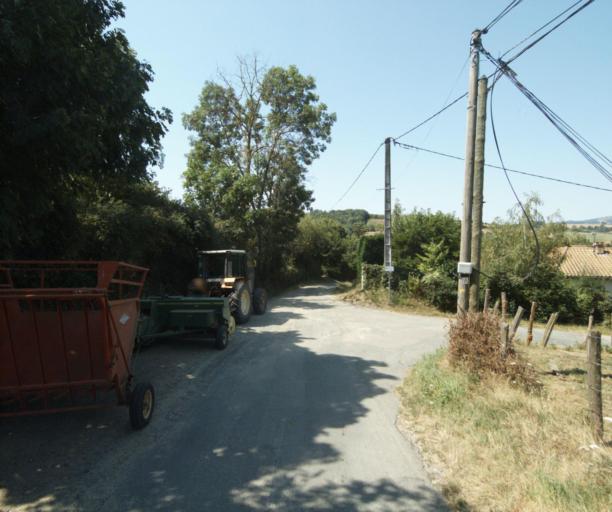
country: FR
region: Rhone-Alpes
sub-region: Departement du Rhone
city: Sourcieux-les-Mines
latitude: 45.7945
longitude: 4.6288
